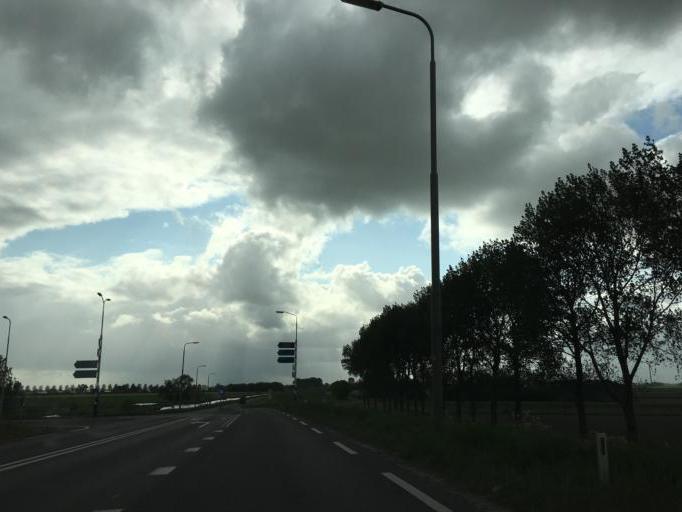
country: NL
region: North Holland
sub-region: Gemeente Medemblik
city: Opperdoes
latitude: 52.7516
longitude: 5.0322
